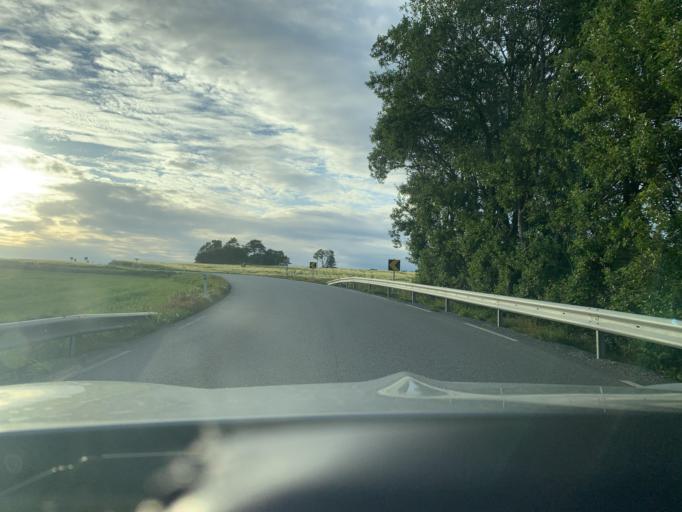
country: NO
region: Rogaland
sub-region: Time
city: Bryne
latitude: 58.7070
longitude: 5.6941
